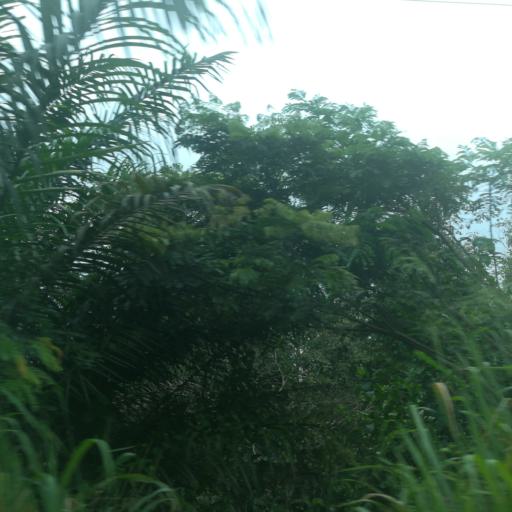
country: NG
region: Lagos
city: Ejirin
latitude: 6.6556
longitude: 3.8009
